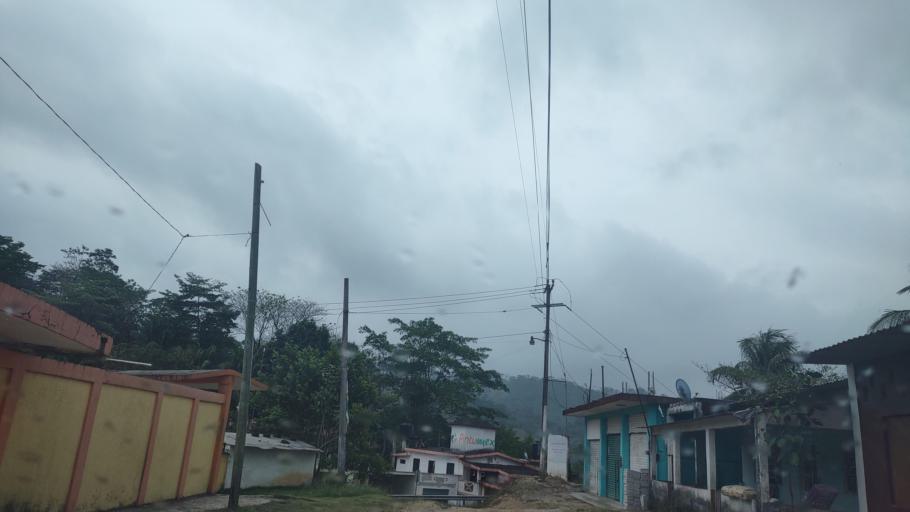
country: MX
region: Veracruz
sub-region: Uxpanapa
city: Poblado 10
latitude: 17.4510
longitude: -94.0967
